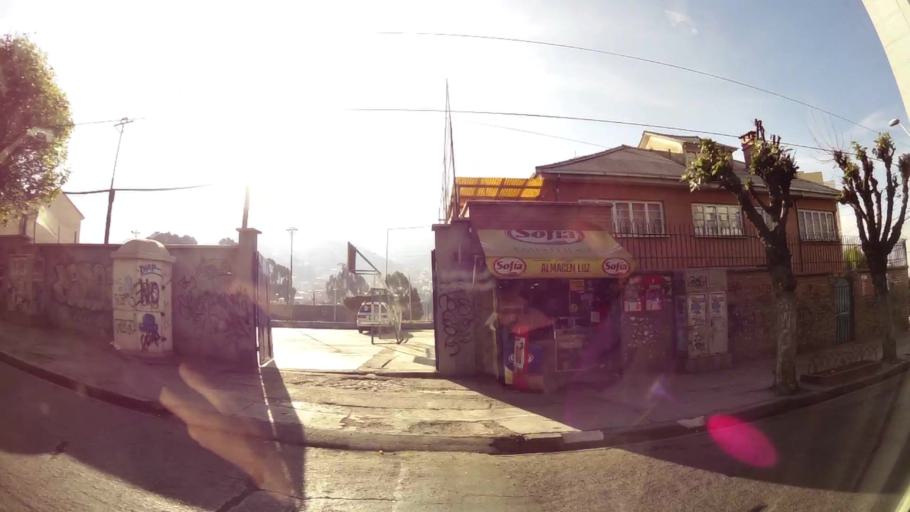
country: BO
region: La Paz
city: La Paz
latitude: -16.4907
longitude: -68.1214
